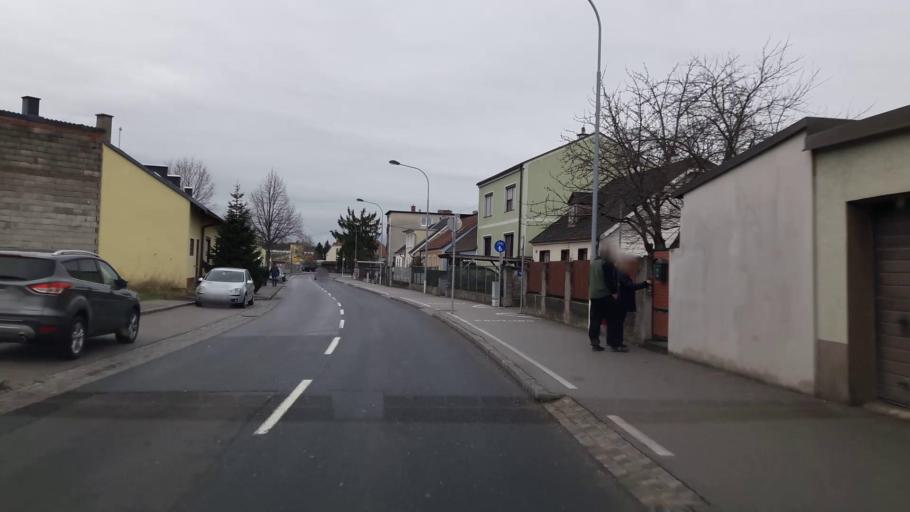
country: AT
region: Burgenland
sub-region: Politischer Bezirk Neusiedl am See
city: Bruckneudorf
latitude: 48.0348
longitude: 16.7830
